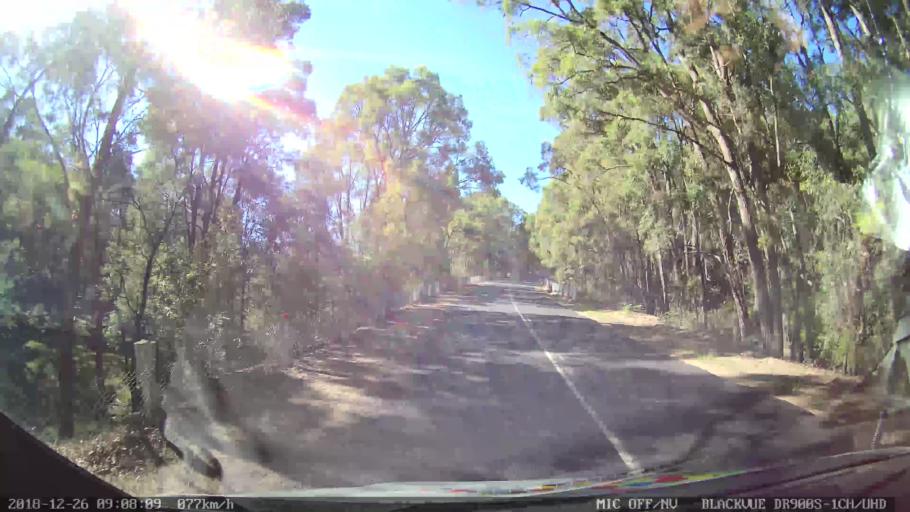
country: AU
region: New South Wales
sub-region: Mid-Western Regional
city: Kandos
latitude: -32.7136
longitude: 150.0032
